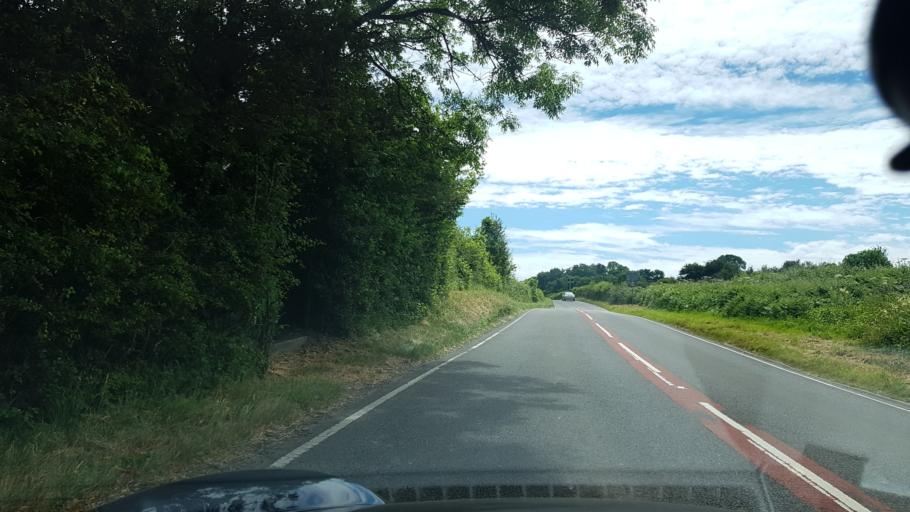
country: GB
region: Wales
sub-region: Carmarthenshire
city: Saint Clears
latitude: 51.8032
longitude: -4.4946
